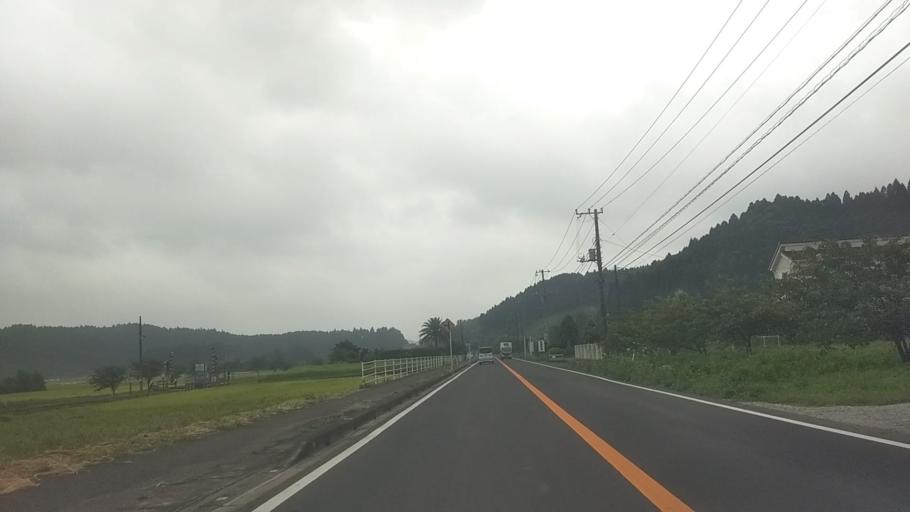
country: JP
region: Chiba
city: Ohara
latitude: 35.2755
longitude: 140.3287
